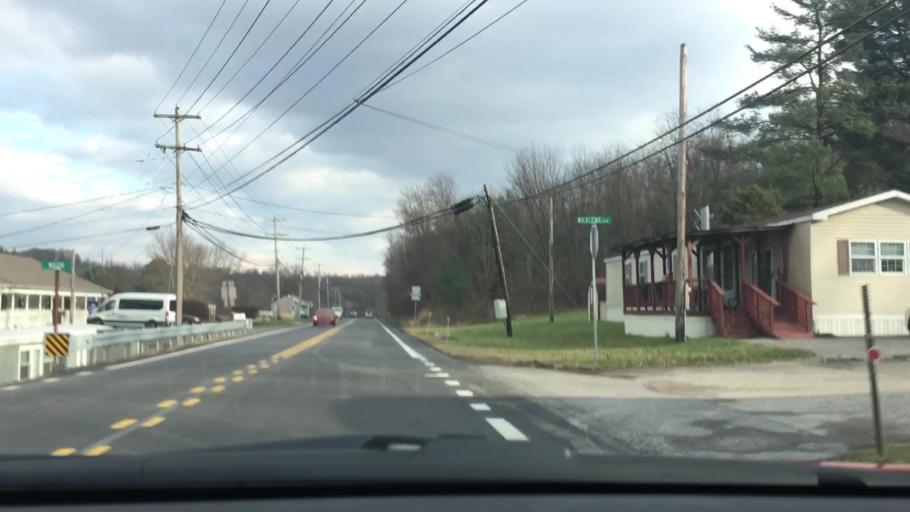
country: US
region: Pennsylvania
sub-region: Allegheny County
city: Oakdale
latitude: 40.4190
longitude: -80.2089
